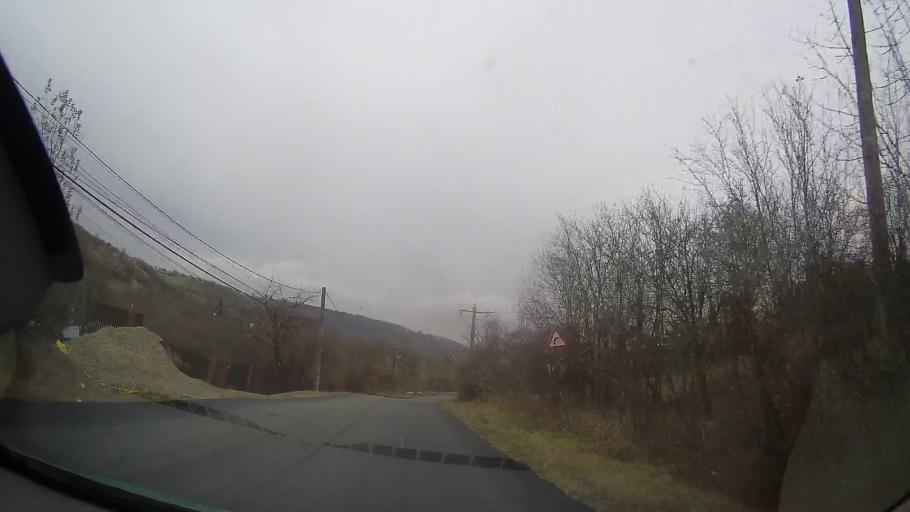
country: RO
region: Prahova
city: Ceptura de Sus
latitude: 45.0485
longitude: 26.3018
